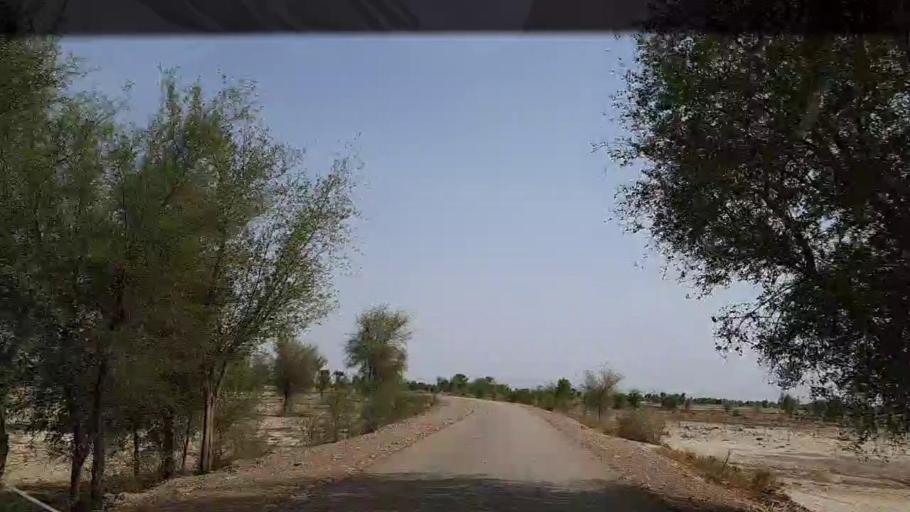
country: PK
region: Sindh
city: Johi
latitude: 26.6453
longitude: 67.5037
